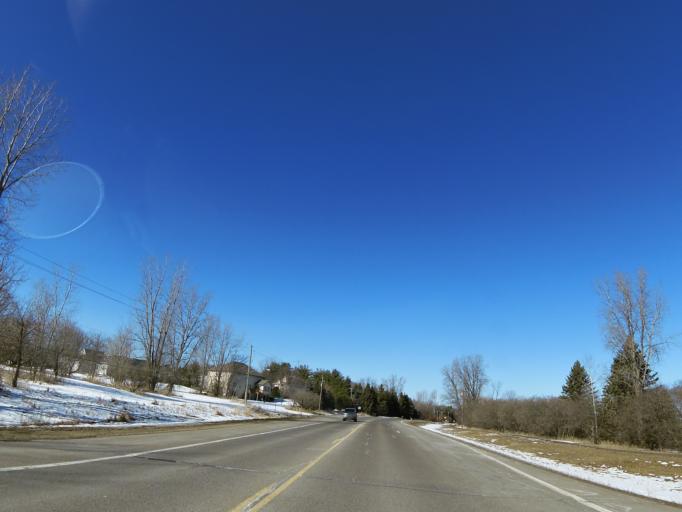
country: US
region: Minnesota
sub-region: Washington County
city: Stillwater
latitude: 45.0730
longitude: -92.8265
